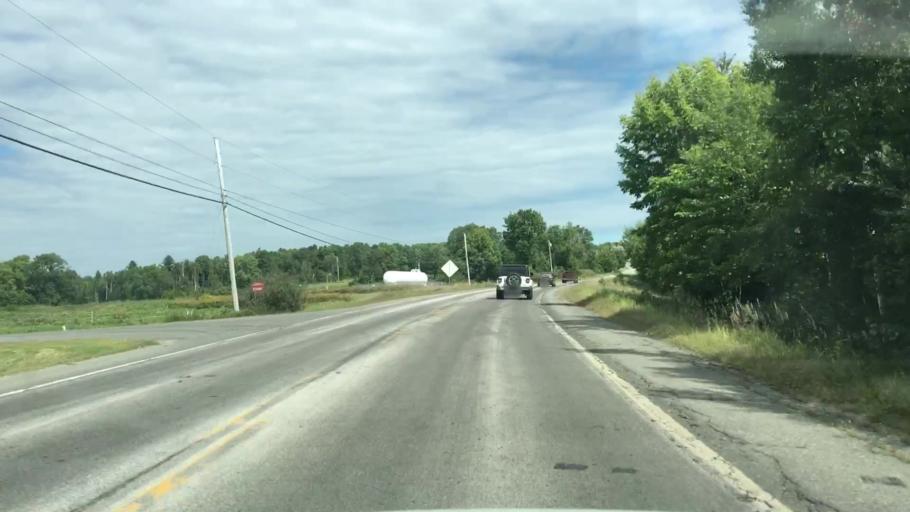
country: US
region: Maine
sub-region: Piscataquis County
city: Dover-Foxcroft
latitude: 45.1539
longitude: -69.2357
